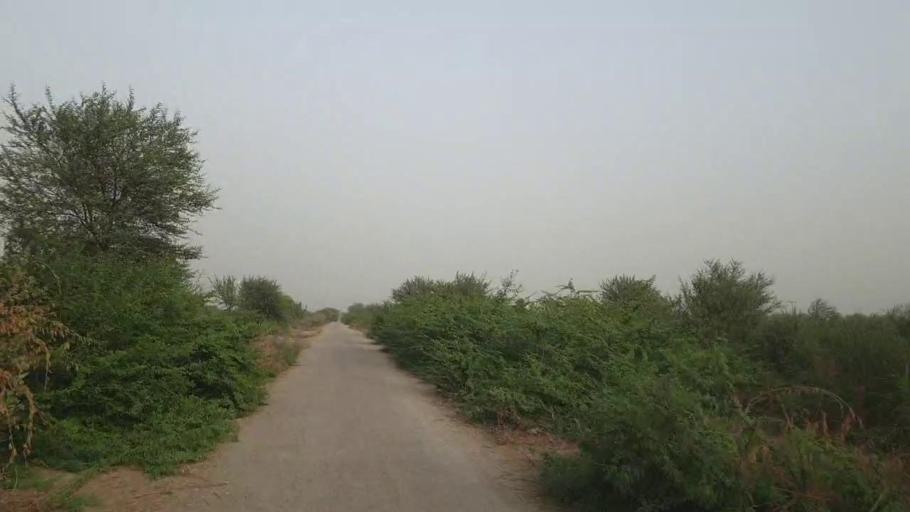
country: PK
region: Sindh
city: Kunri
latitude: 25.1078
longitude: 69.5230
